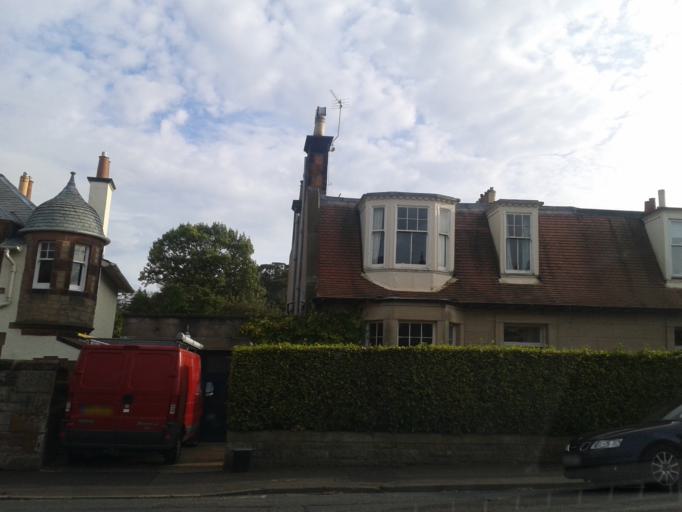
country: GB
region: Scotland
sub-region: Edinburgh
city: Edinburgh
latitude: 55.9199
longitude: -3.2110
